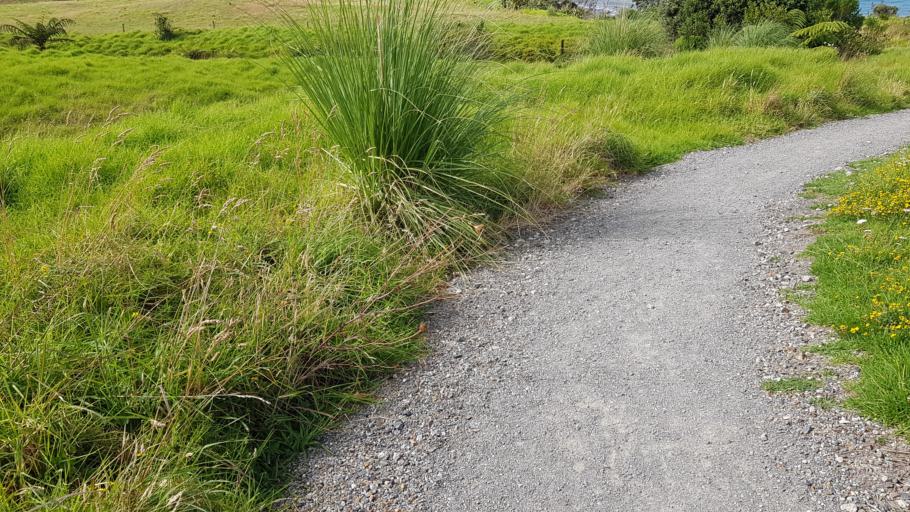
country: NZ
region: Auckland
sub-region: Auckland
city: Rothesay Bay
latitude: -36.6704
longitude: 174.7461
